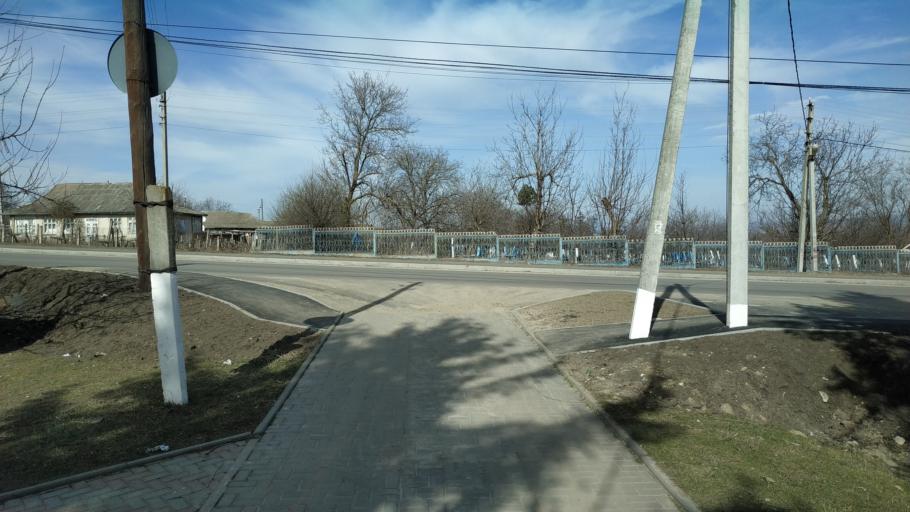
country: RO
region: Iasi
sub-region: Comuna Grozesti
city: Grozesti
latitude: 46.9638
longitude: 28.1602
